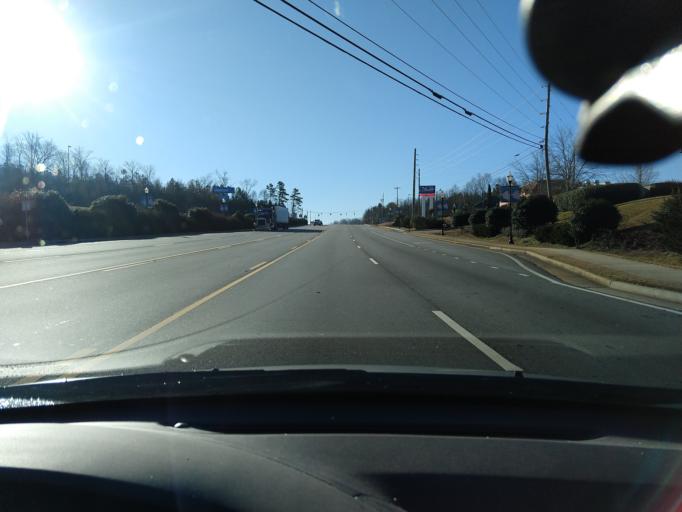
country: US
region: Georgia
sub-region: Jackson County
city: Commerce
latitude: 34.2474
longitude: -83.4595
